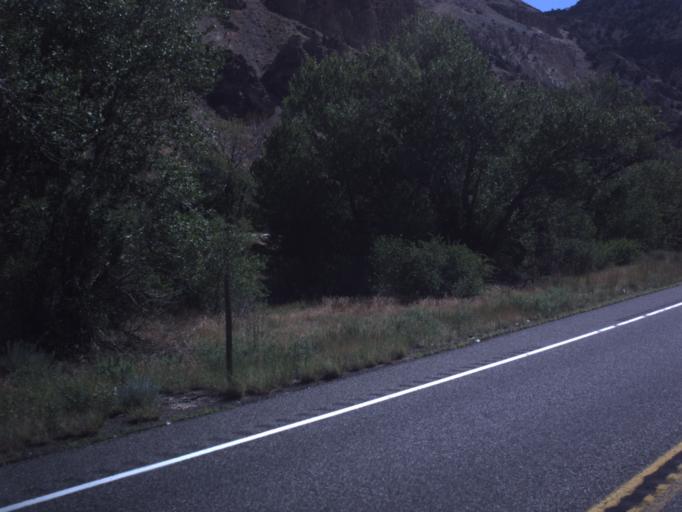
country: US
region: Utah
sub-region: Sevier County
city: Monroe
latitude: 38.5713
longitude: -112.2564
